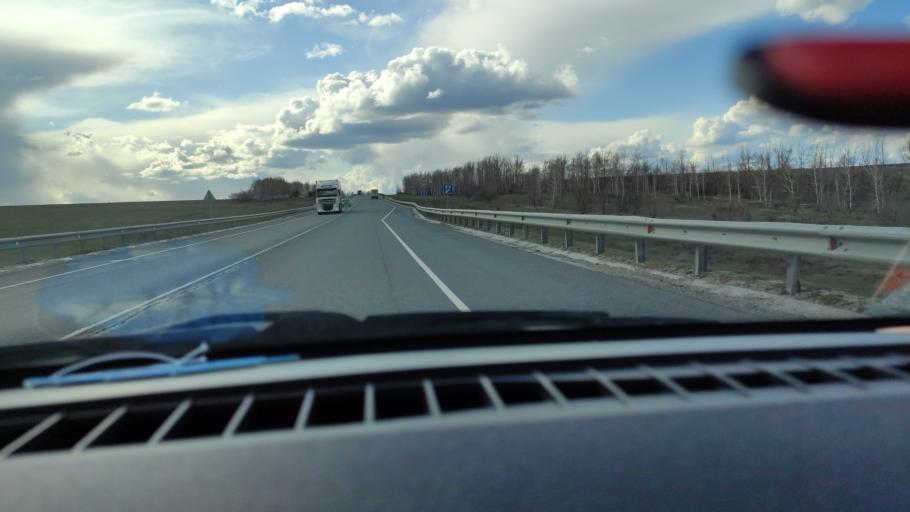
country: RU
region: Saratov
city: Shikhany
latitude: 52.1203
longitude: 47.2650
